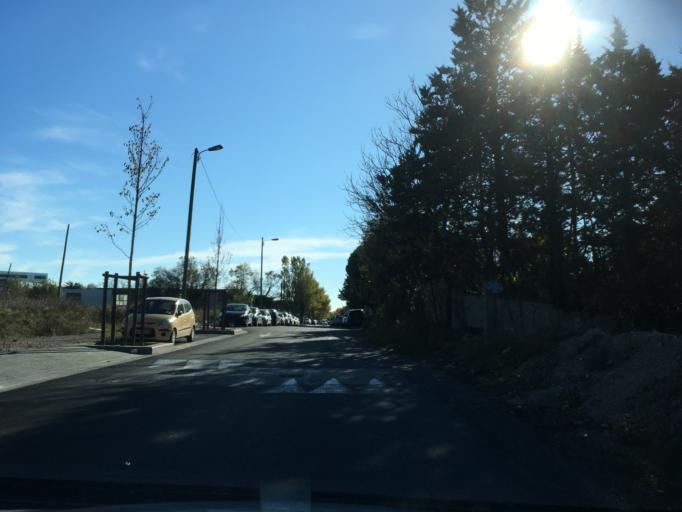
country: FR
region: Languedoc-Roussillon
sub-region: Departement de l'Herault
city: Juvignac
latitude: 43.6231
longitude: 3.8213
